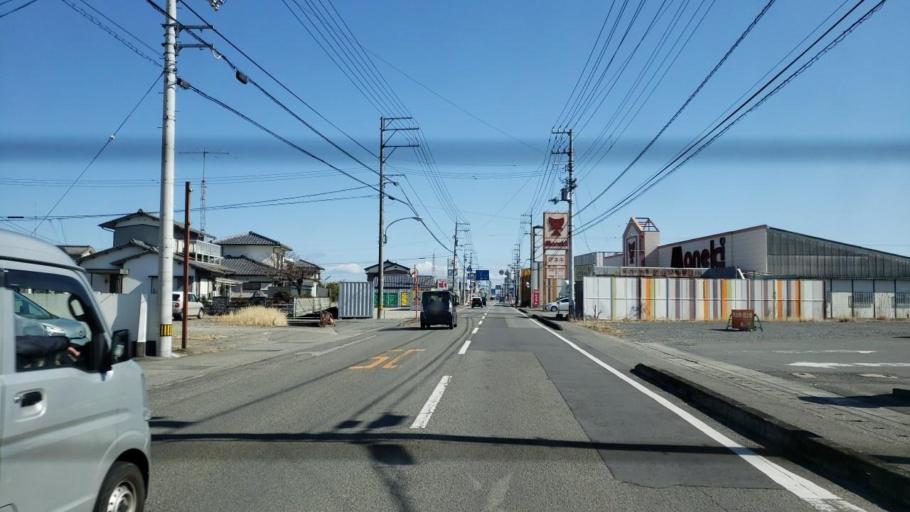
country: JP
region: Tokushima
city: Tokushima-shi
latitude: 34.1336
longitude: 134.5124
